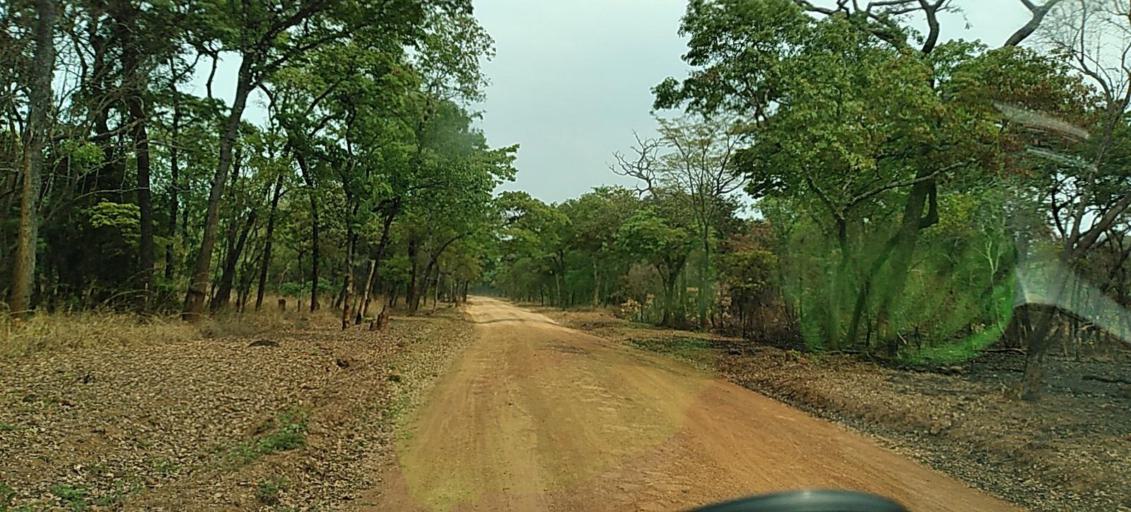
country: ZM
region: North-Western
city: Solwezi
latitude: -12.9428
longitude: 26.5582
